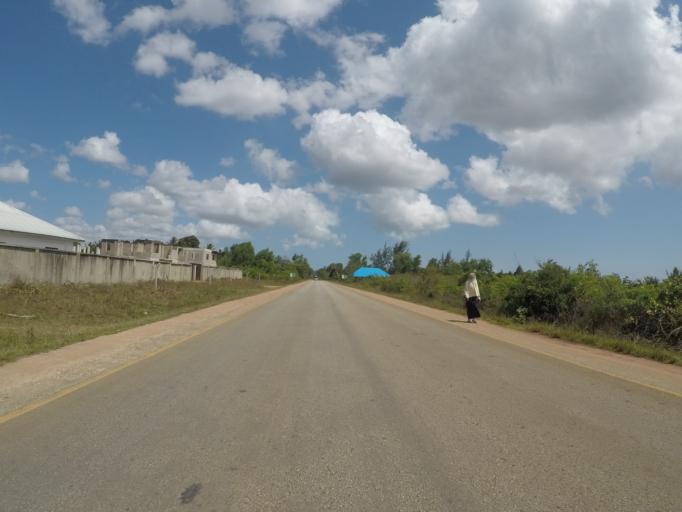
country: TZ
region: Zanzibar Central/South
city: Koani
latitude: -6.1615
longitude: 39.3299
